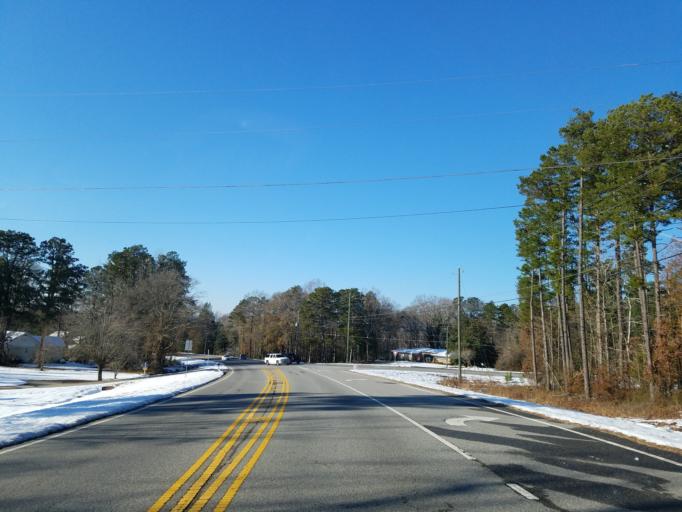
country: US
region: Georgia
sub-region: Dawson County
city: Dawsonville
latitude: 34.3315
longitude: -84.1059
